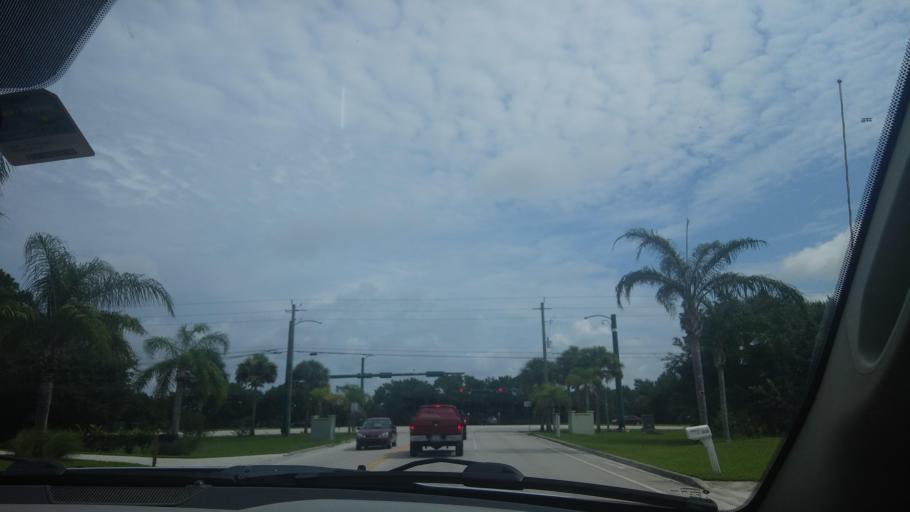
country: US
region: Florida
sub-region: Indian River County
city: Fellsmere
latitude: 27.7661
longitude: -80.5337
